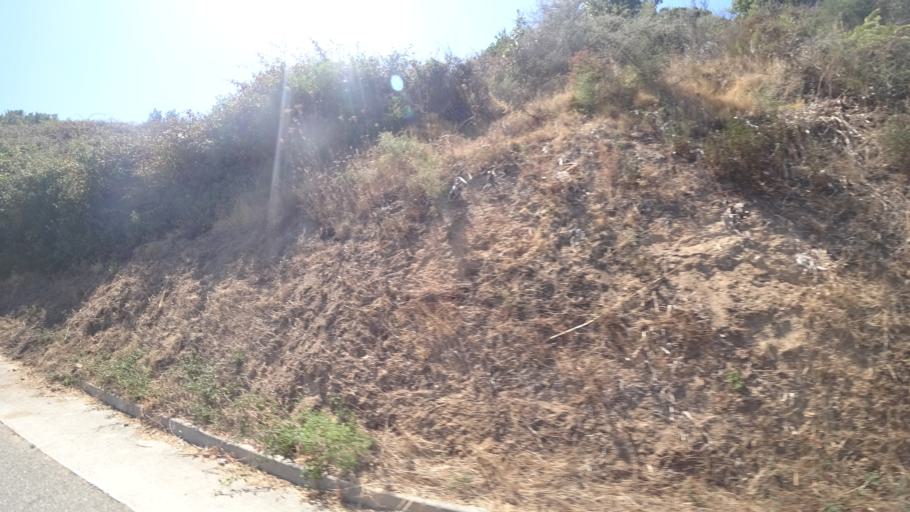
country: FR
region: Corsica
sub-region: Departement de la Corse-du-Sud
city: Alata
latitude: 41.9762
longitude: 8.6831
